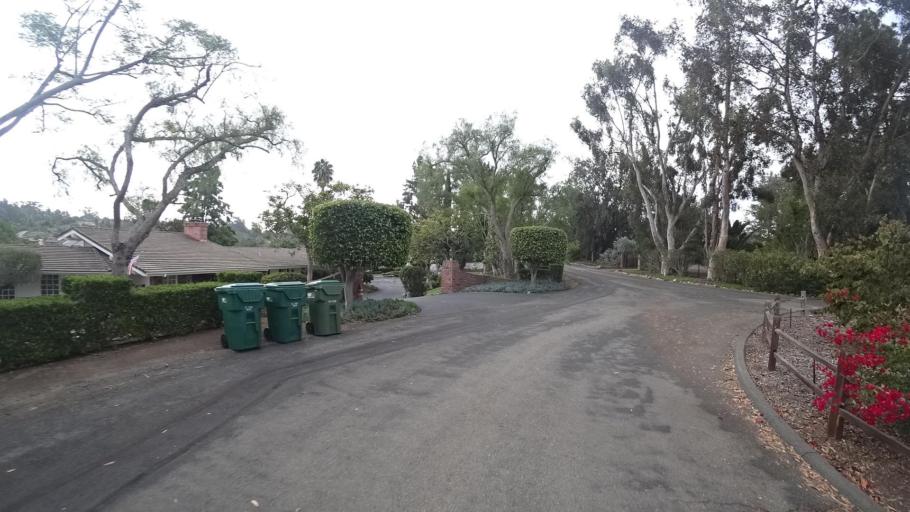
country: US
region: California
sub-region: San Diego County
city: Rancho Santa Fe
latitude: 33.0390
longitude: -117.2238
